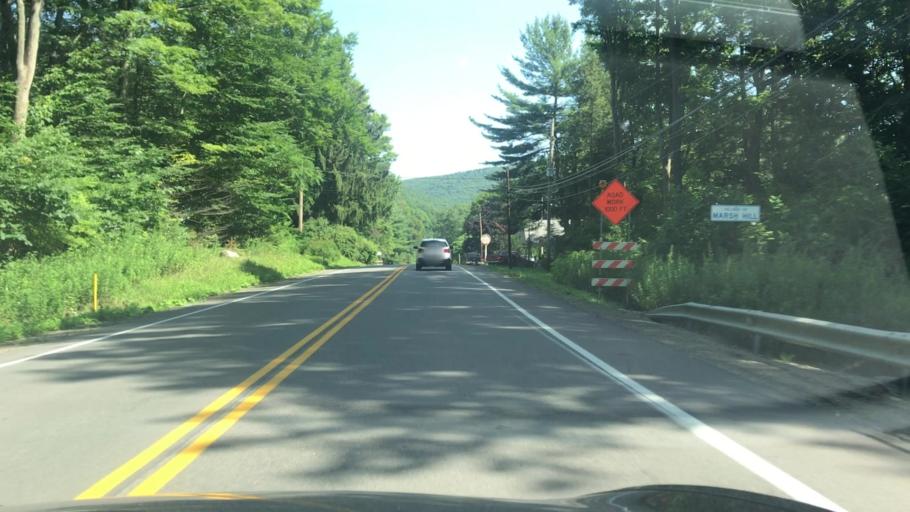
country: US
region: Pennsylvania
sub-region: Lycoming County
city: Kenmar
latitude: 41.4725
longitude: -76.9810
